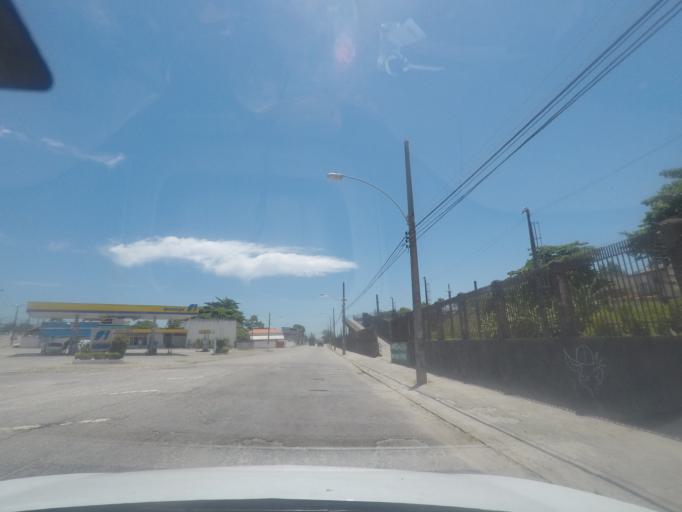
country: BR
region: Rio de Janeiro
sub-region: Itaguai
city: Itaguai
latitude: -22.9196
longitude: -43.6891
